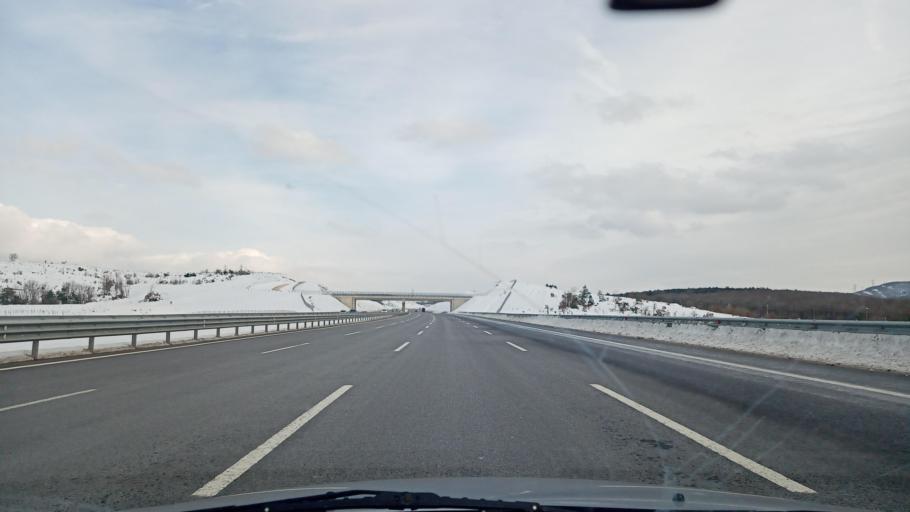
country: TR
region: Kocaeli
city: Hereke
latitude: 40.8948
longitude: 29.6218
